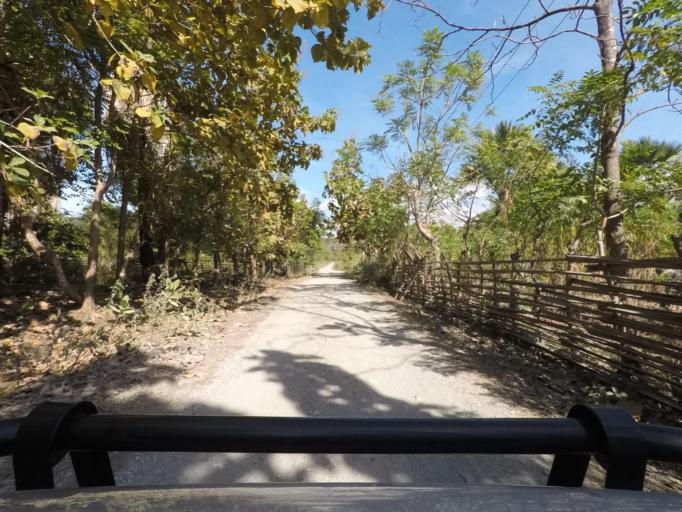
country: ID
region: East Nusa Tenggara
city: Atambua
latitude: -8.9566
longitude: 124.9598
